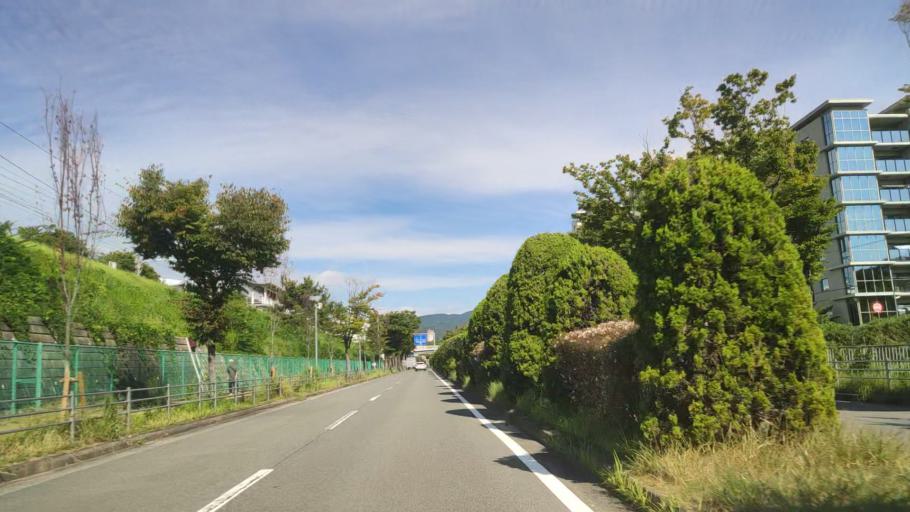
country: JP
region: Osaka
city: Mino
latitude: 34.8185
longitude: 135.5122
